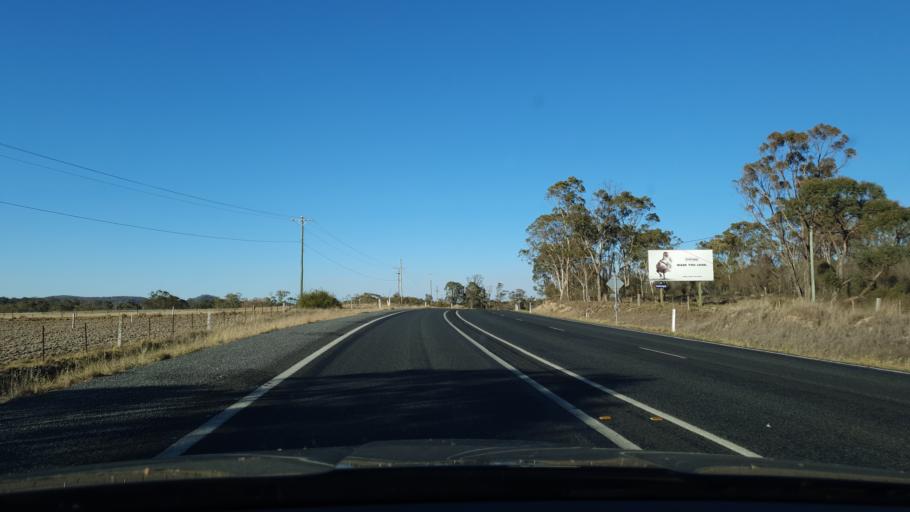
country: AU
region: Queensland
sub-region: Southern Downs
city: Stanthorpe
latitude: -28.6872
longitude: 151.9118
